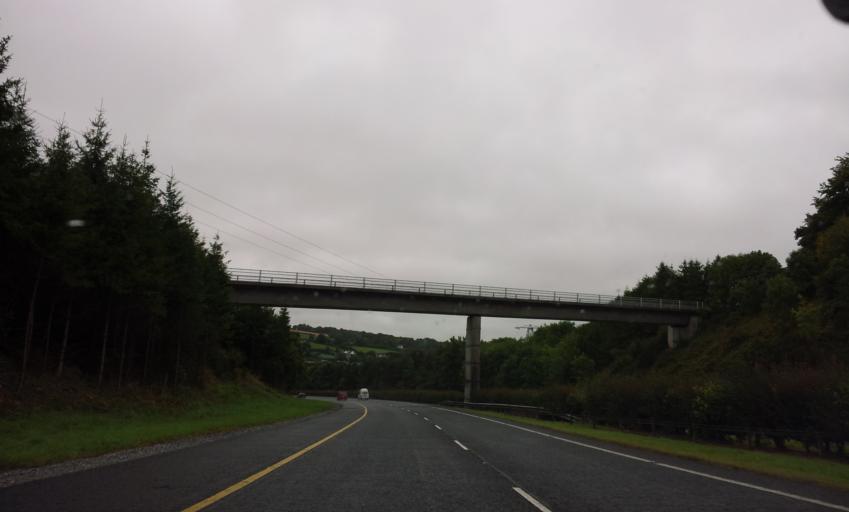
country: IE
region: Munster
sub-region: County Cork
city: Passage West
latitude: 51.9263
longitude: -8.3780
